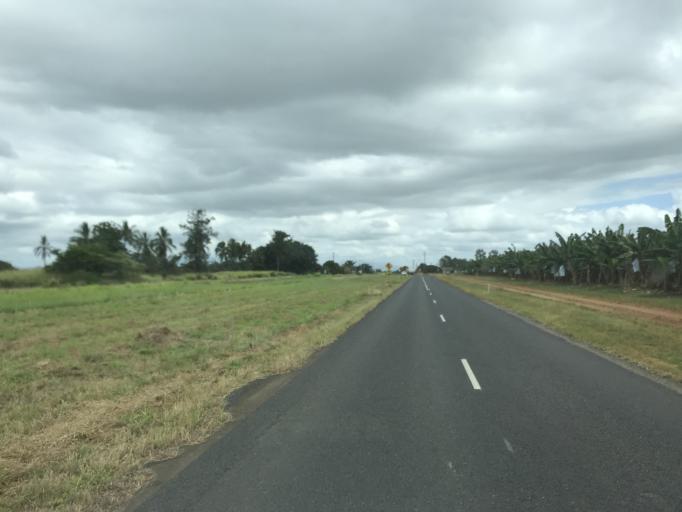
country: AU
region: Queensland
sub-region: Cassowary Coast
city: Innisfail
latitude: -17.6084
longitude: 146.0135
